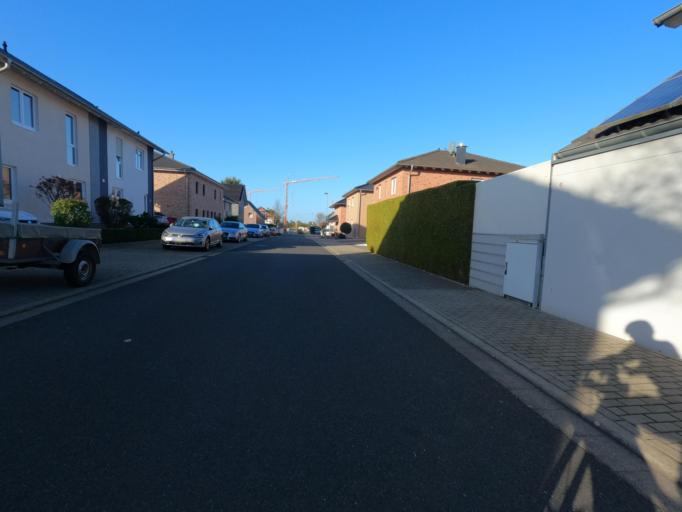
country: DE
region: North Rhine-Westphalia
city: Erkelenz
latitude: 51.0821
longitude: 6.2956
